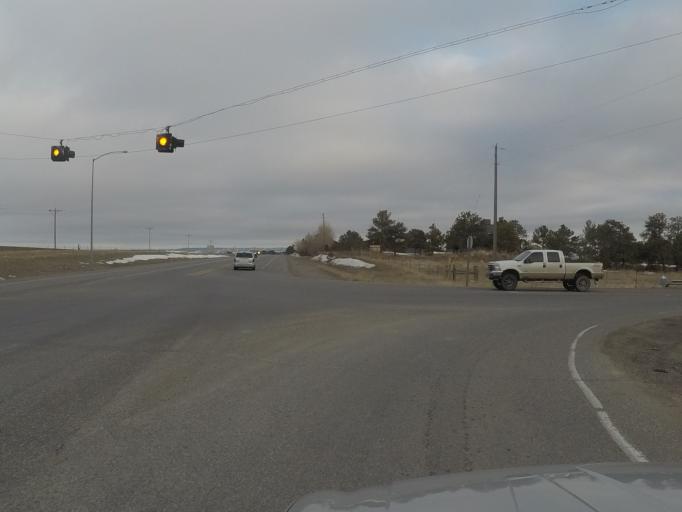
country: US
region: Montana
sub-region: Yellowstone County
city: Billings
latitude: 45.8064
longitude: -108.6002
